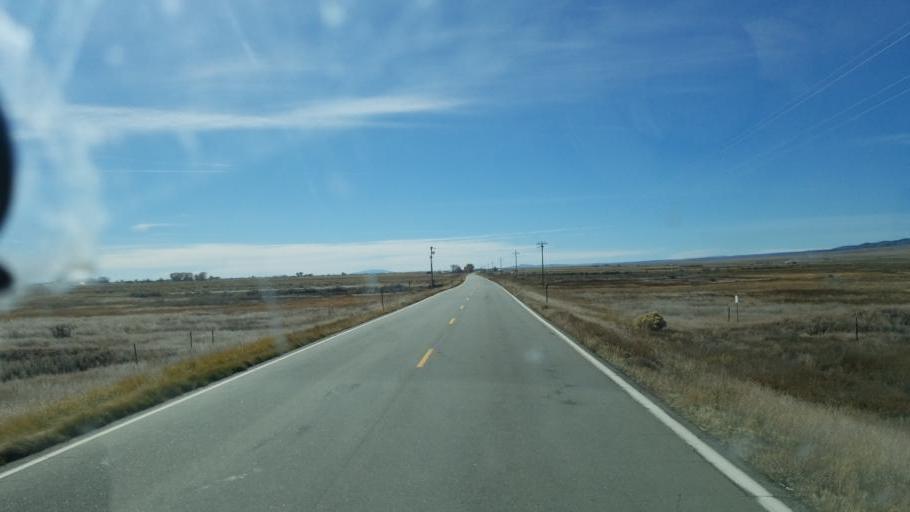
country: US
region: Colorado
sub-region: Rio Grande County
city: Monte Vista
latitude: 37.4747
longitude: -106.1488
